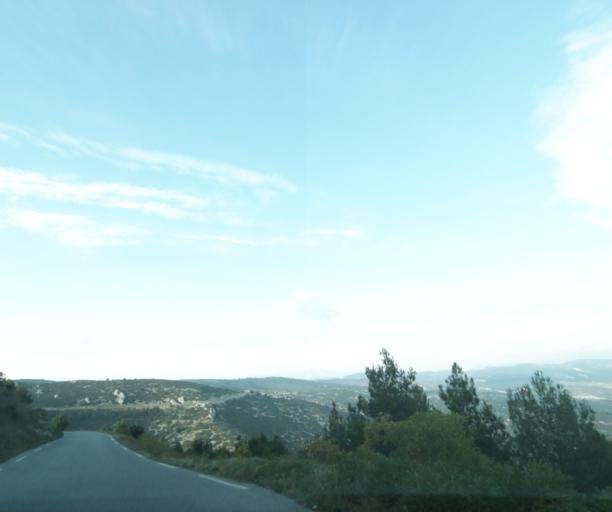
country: FR
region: Provence-Alpes-Cote d'Azur
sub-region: Departement des Bouches-du-Rhone
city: Cassis
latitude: 43.1841
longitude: 5.5662
